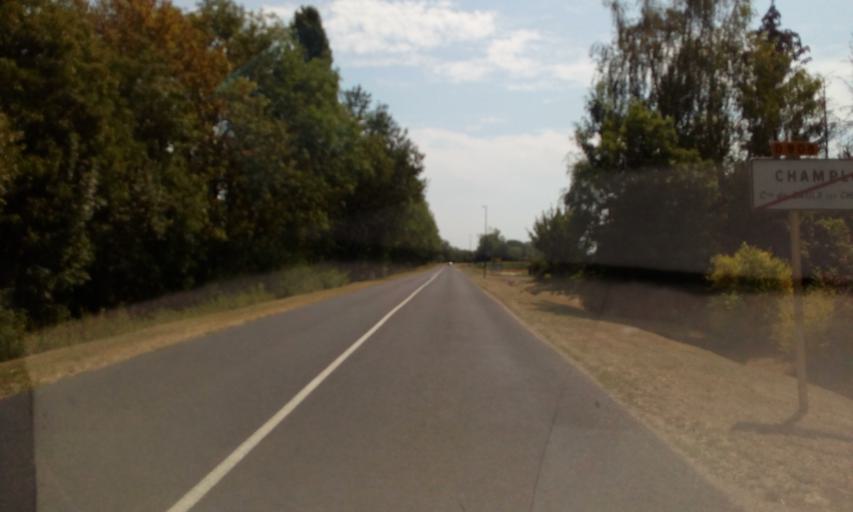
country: FR
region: Lorraine
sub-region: Departement de la Meuse
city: Vigneulles-les-Hattonchatel
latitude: 49.0779
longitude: 5.6406
